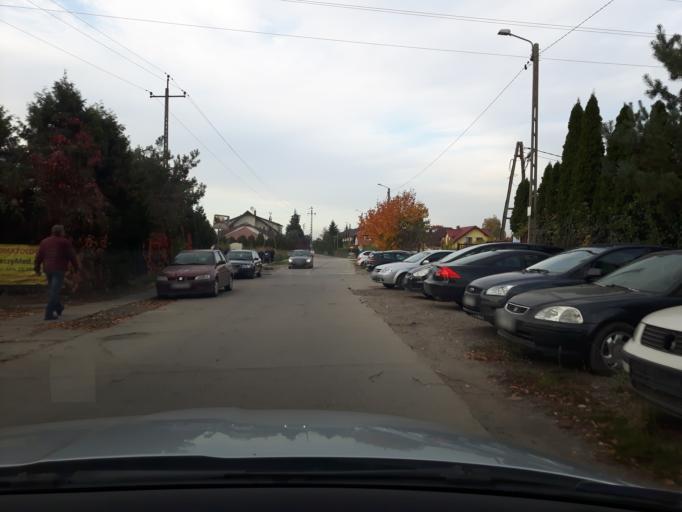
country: PL
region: Masovian Voivodeship
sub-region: Powiat wolominski
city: Zabki
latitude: 52.2800
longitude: 21.1189
